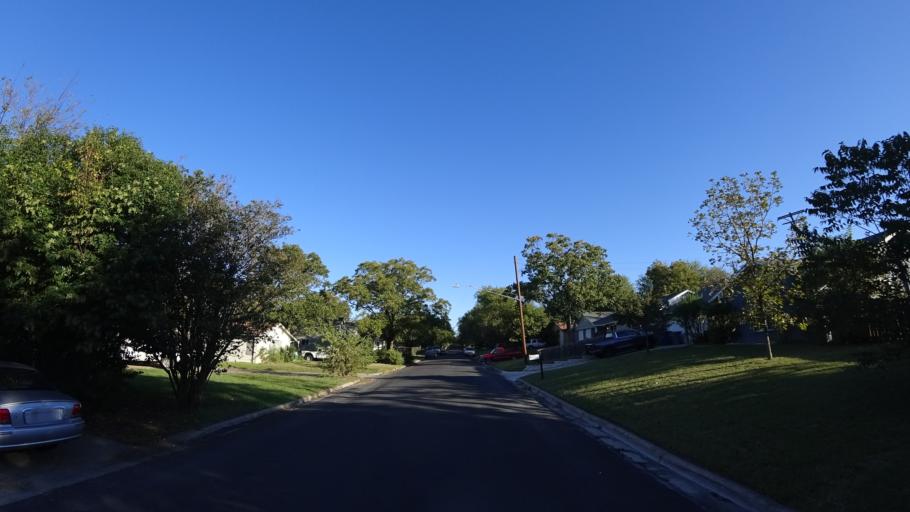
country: US
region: Texas
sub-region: Travis County
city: Austin
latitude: 30.3023
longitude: -97.6845
